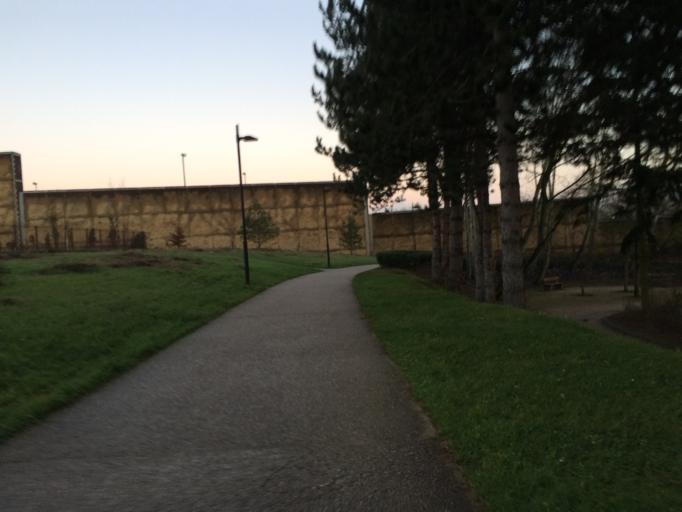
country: FR
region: Ile-de-France
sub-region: Departement des Hauts-de-Seine
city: Sceaux
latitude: 48.7598
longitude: 2.2844
